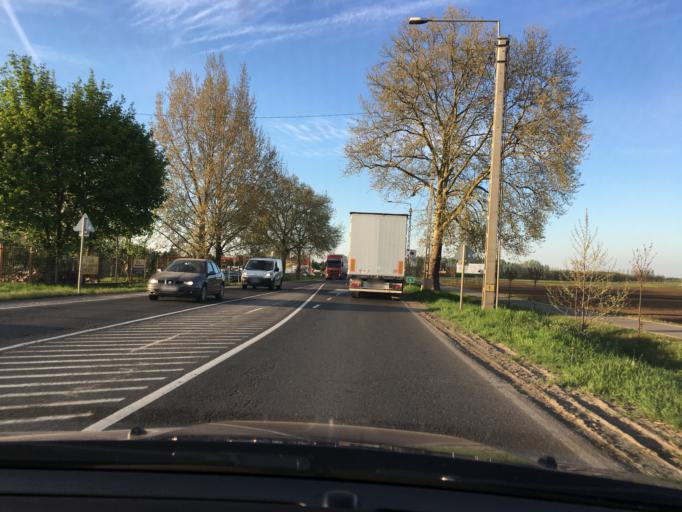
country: HU
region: Hajdu-Bihar
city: Mikepercs
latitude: 47.4509
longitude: 21.6331
